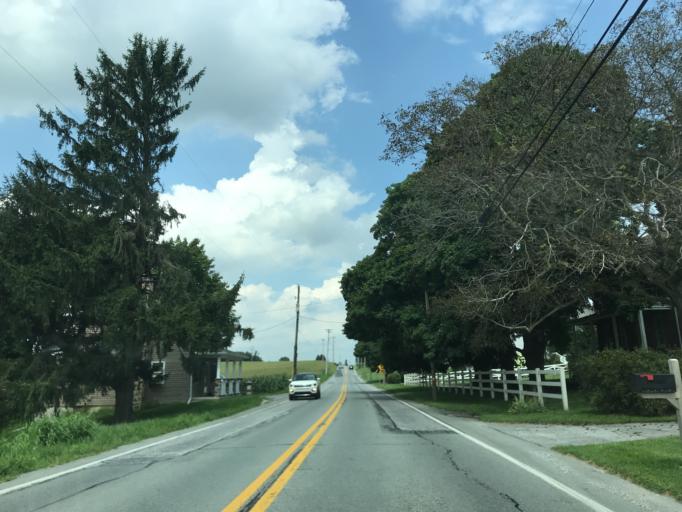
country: US
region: Pennsylvania
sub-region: York County
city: Red Lion
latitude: 39.8721
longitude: -76.6149
